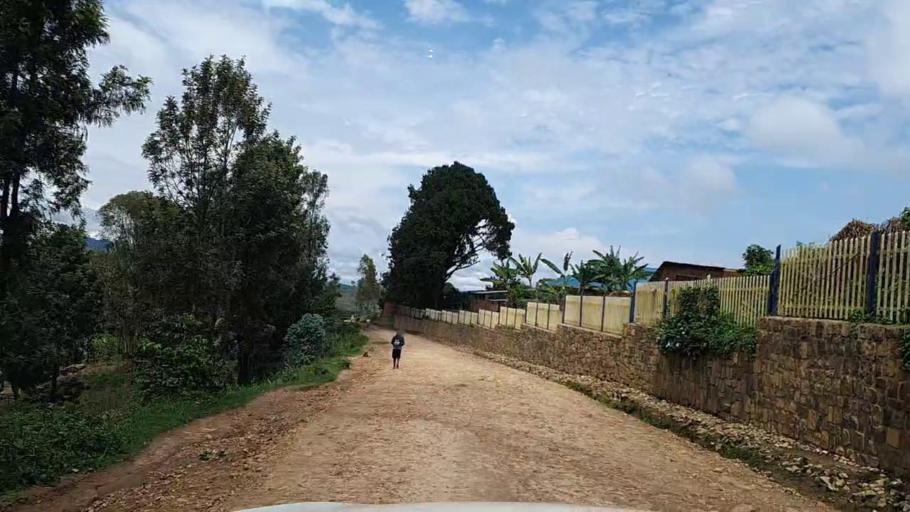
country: RW
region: Southern Province
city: Gikongoro
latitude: -2.3346
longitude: 29.5231
